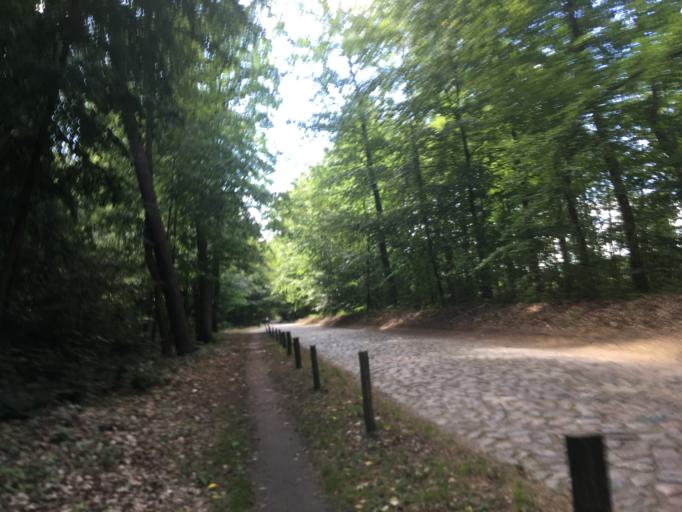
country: DE
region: Brandenburg
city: Oderberg
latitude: 52.9103
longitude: 14.0114
